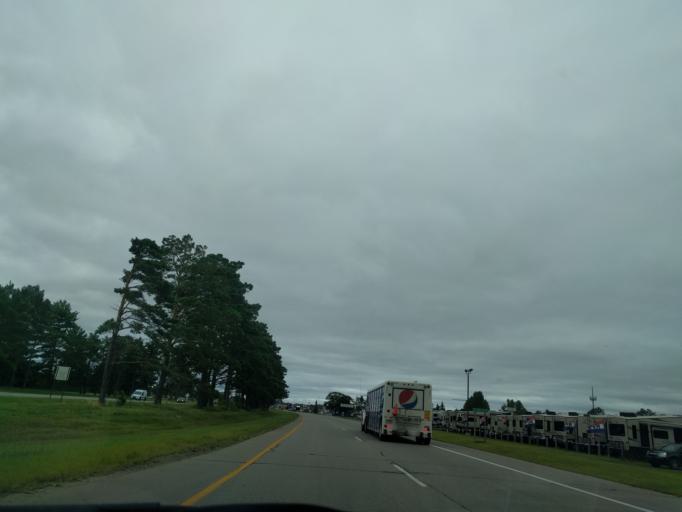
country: US
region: Michigan
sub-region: Delta County
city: Escanaba
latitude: 45.7846
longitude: -87.0830
